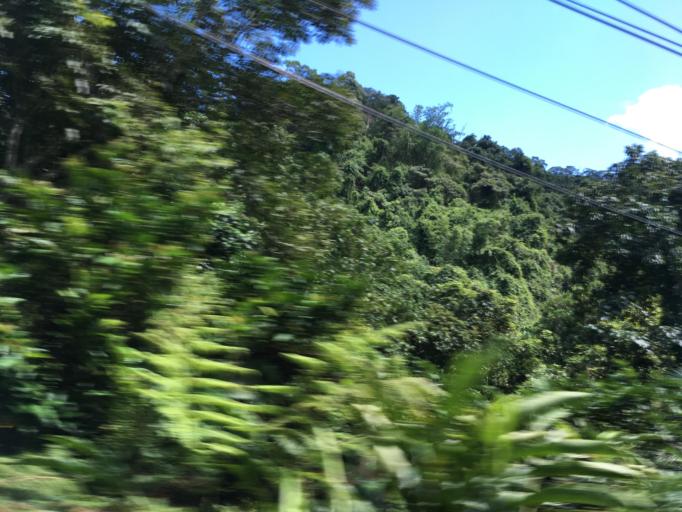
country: TW
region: Taipei
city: Taipei
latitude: 24.9489
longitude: 121.5554
